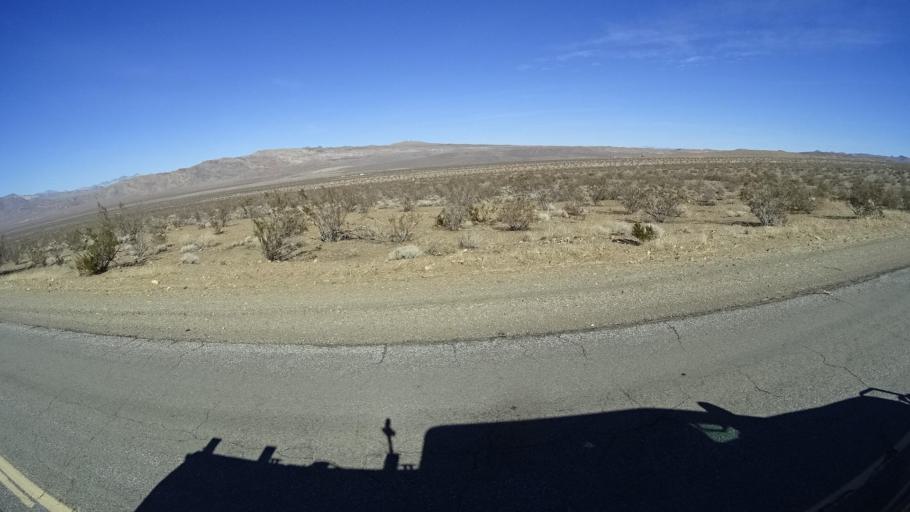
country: US
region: California
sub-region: Kern County
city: Ridgecrest
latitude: 35.3811
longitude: -117.6846
